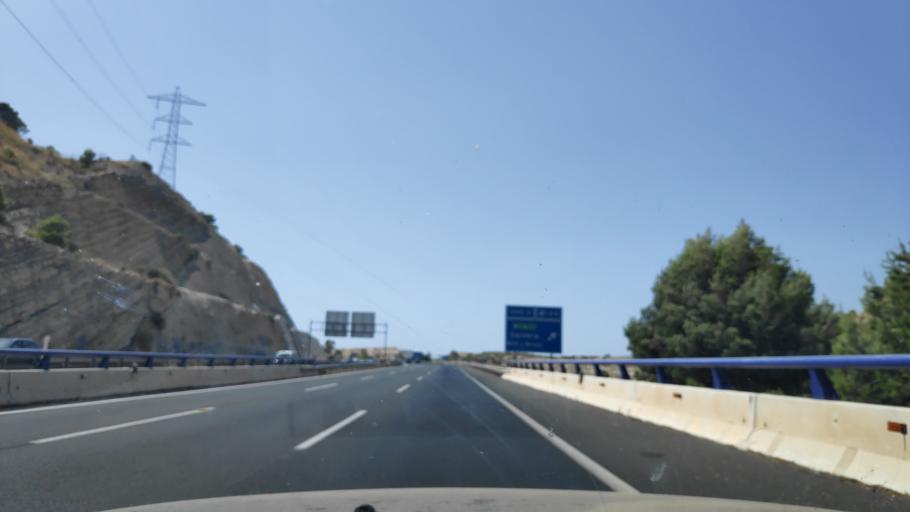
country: ES
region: Murcia
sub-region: Murcia
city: Murcia
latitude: 37.8732
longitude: -1.1265
